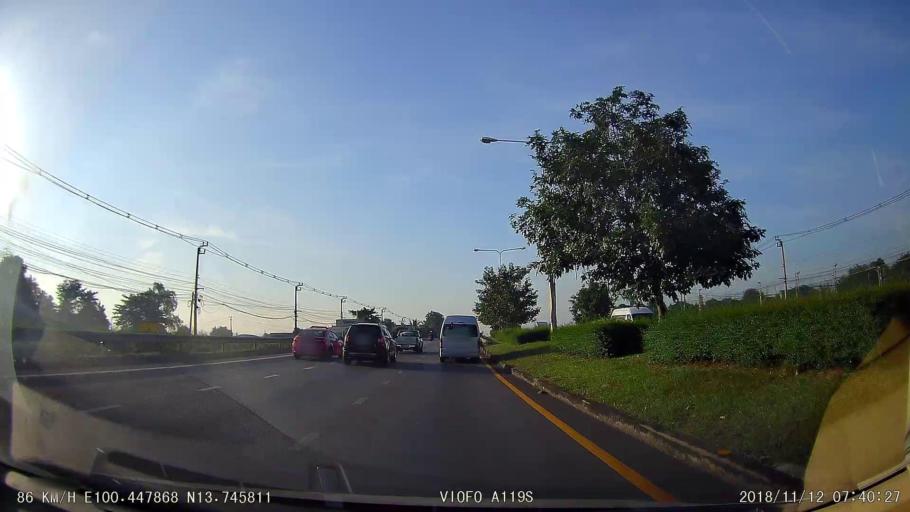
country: TH
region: Bangkok
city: Taling Chan
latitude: 13.7457
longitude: 100.4479
